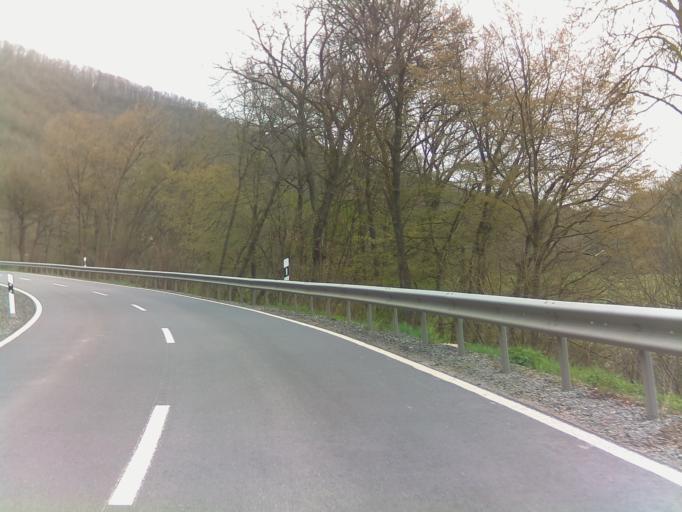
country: DE
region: Rheinland-Pfalz
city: Bruschied
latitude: 49.8205
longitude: 7.3988
